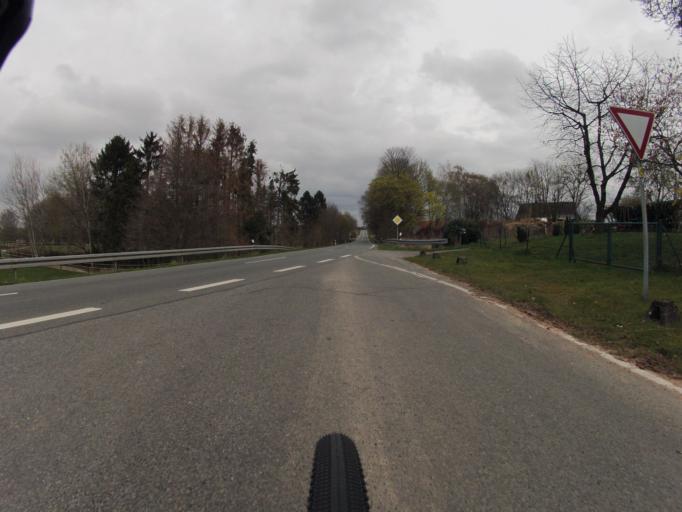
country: DE
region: North Rhine-Westphalia
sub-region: Regierungsbezirk Munster
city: Tecklenburg
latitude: 52.2736
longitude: 7.8316
